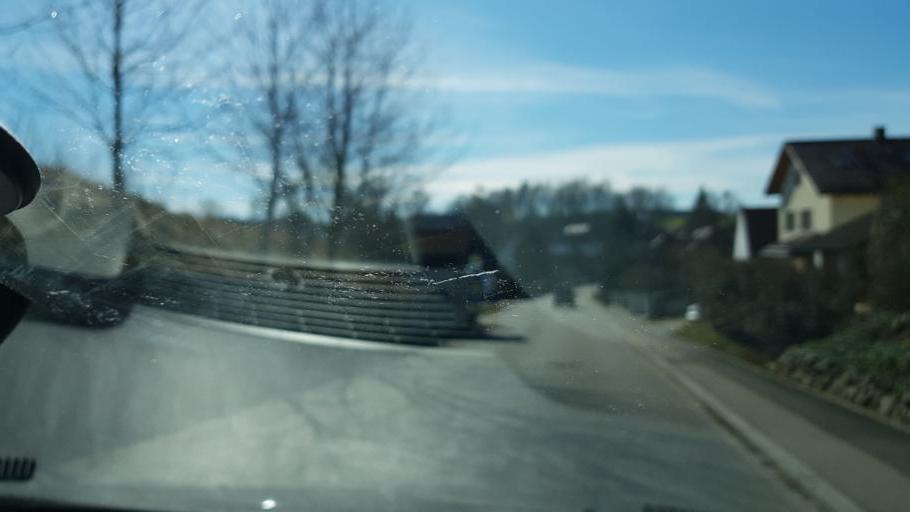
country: DE
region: Bavaria
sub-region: Upper Bavaria
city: Oberschweinbach
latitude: 48.2427
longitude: 11.1451
